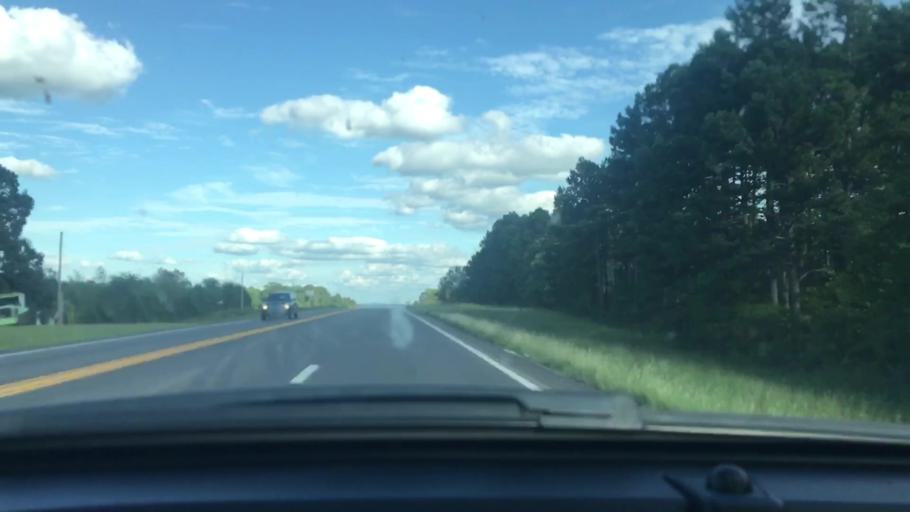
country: US
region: Missouri
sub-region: Oregon County
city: Thayer
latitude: 36.5830
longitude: -91.6115
